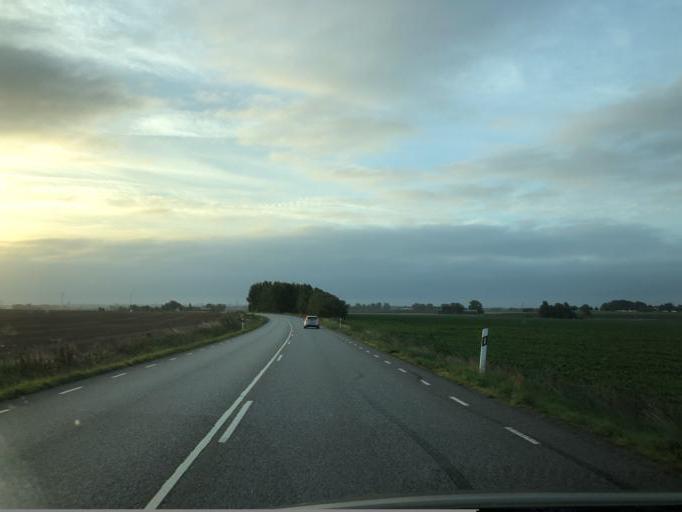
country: SE
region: Skane
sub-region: Kavlinge Kommun
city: Kaevlinge
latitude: 55.7613
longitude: 13.1103
